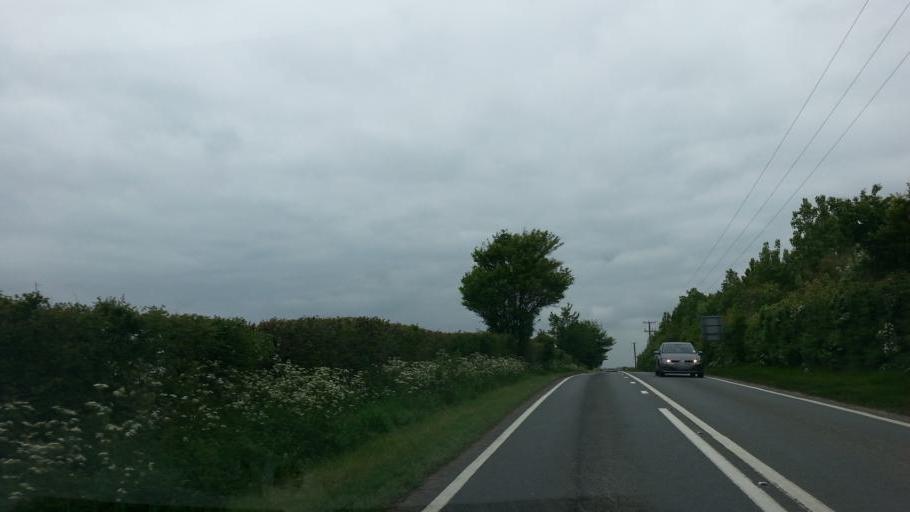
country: GB
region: England
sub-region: Suffolk
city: Bury St Edmunds
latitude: 52.2628
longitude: 0.6794
